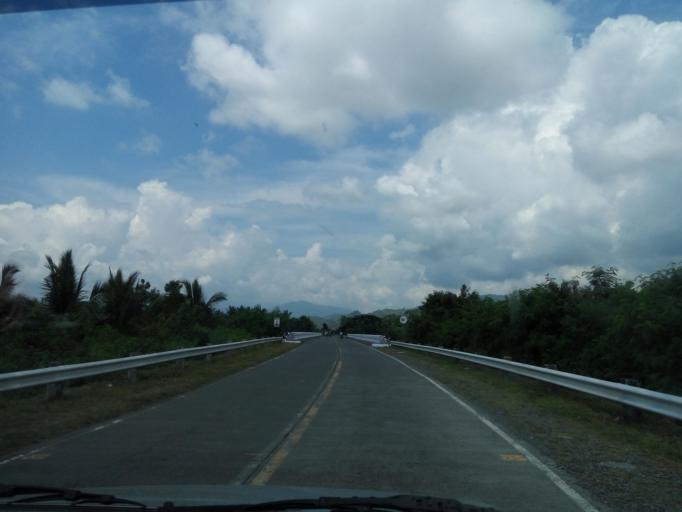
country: PH
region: Central Luzon
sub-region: Province of Aurora
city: Maria Aurora
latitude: 15.8024
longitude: 121.4548
